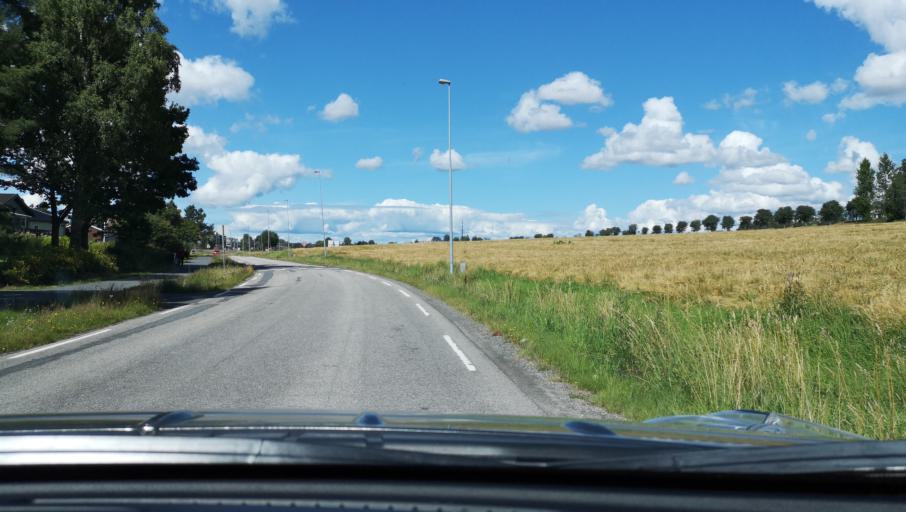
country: NO
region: Akershus
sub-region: As
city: As
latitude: 59.6565
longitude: 10.7994
